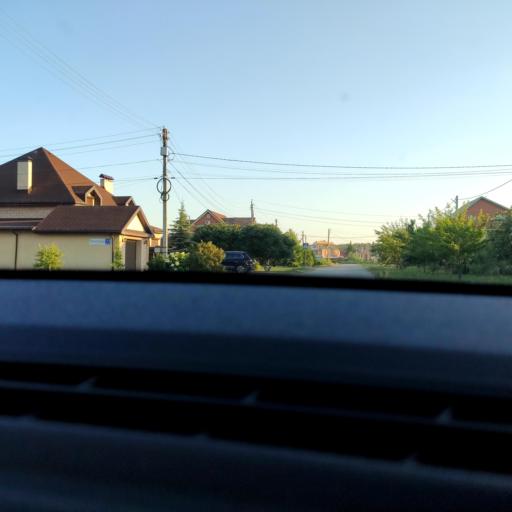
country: RU
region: Samara
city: Podstepki
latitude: 53.5778
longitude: 49.0682
